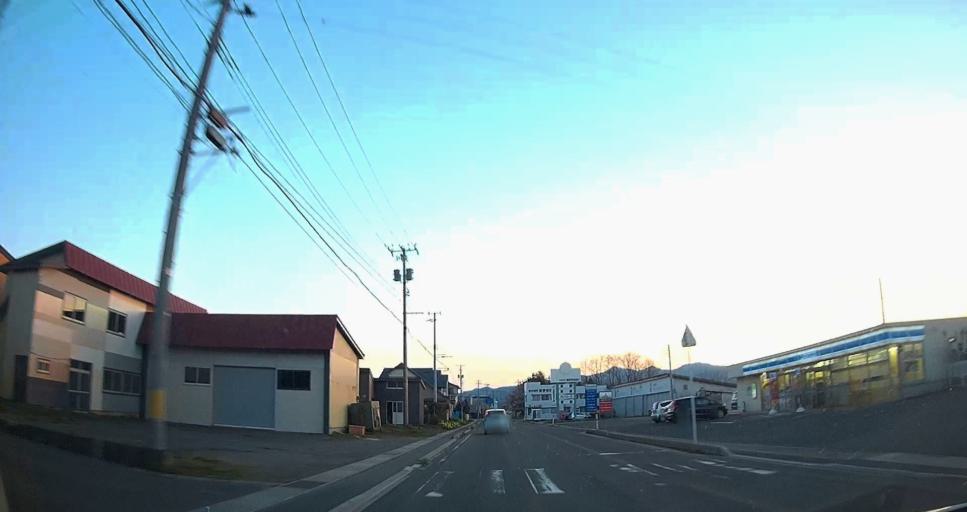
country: JP
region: Aomori
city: Misawa
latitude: 40.8739
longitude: 141.1366
